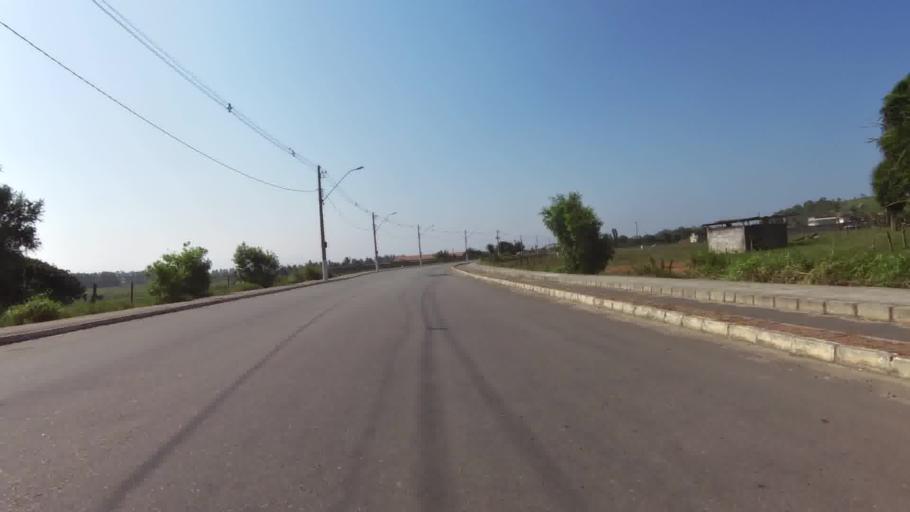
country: BR
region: Espirito Santo
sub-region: Itapemirim
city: Itapemirim
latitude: -21.0179
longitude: -40.8398
